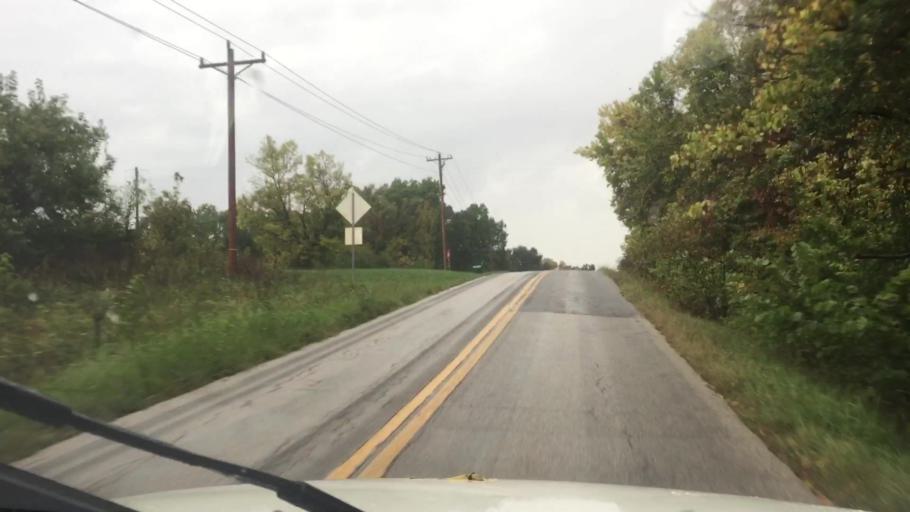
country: US
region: Missouri
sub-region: Boone County
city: Columbia
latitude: 38.9327
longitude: -92.4916
